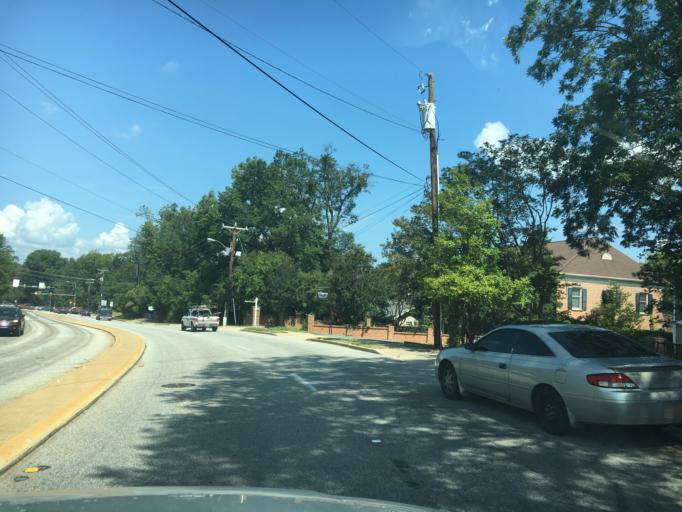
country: US
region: South Carolina
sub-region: Greenville County
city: Greenville
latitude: 34.8531
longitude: -82.3904
